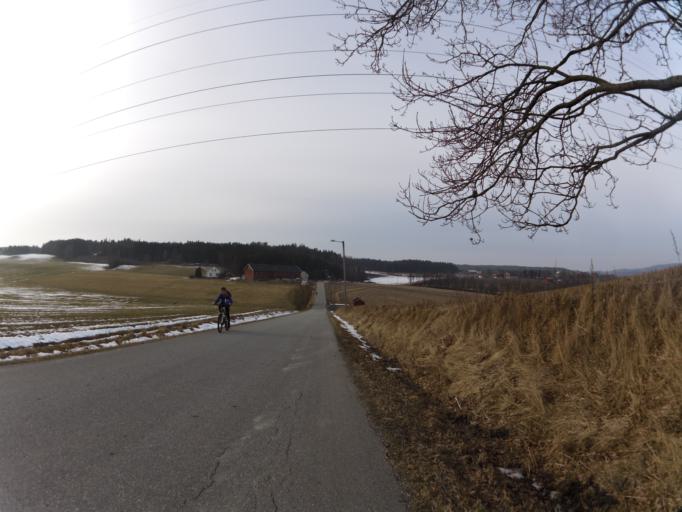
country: NO
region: Ostfold
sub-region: Fredrikstad
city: Fredrikstad
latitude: 59.2731
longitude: 11.0073
